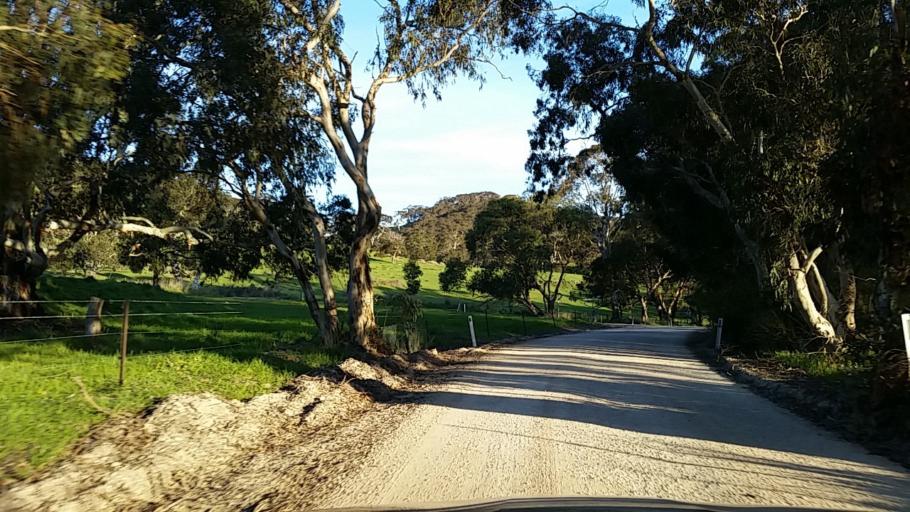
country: AU
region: South Australia
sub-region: Alexandrina
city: Mount Compass
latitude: -35.3157
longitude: 138.6701
